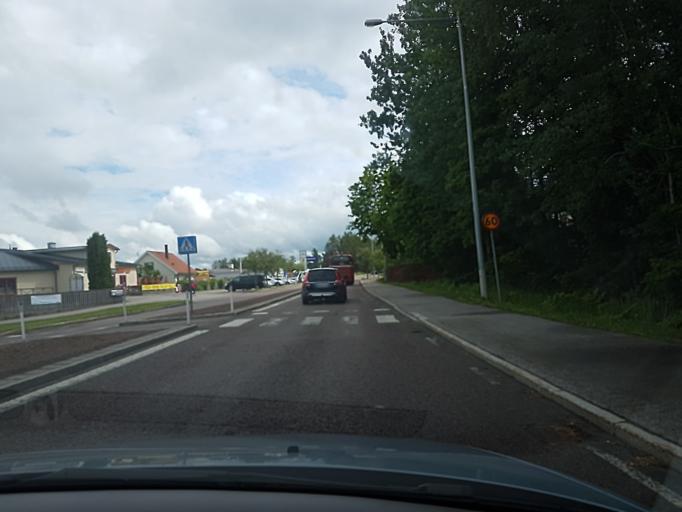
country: SE
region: Uppsala
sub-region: Osthammars Kommun
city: OEsthammar
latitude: 60.2548
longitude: 18.3456
